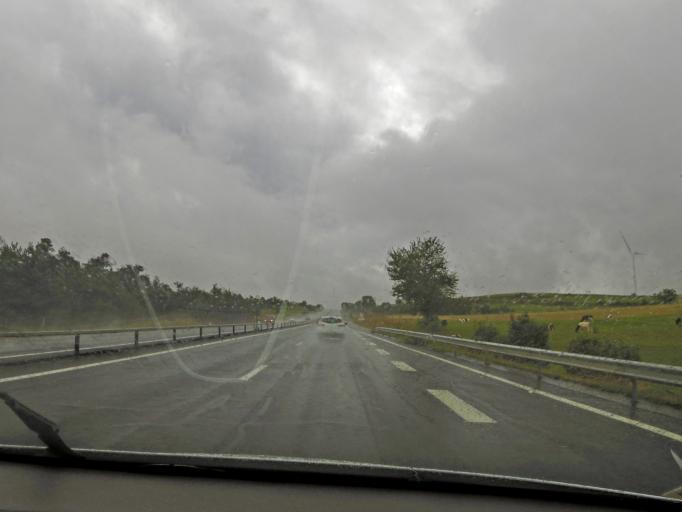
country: FR
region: Auvergne
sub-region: Departement du Cantal
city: Saint-Flour
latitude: 45.1122
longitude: 3.1378
